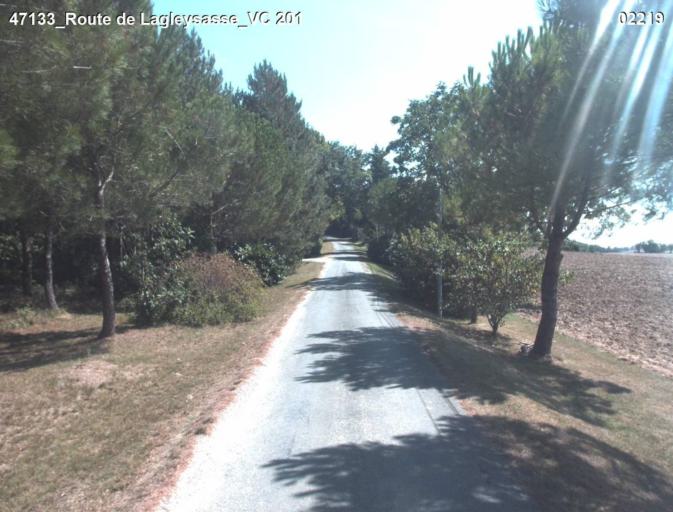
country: FR
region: Aquitaine
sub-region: Departement du Lot-et-Garonne
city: Laplume
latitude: 44.0607
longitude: 0.5329
